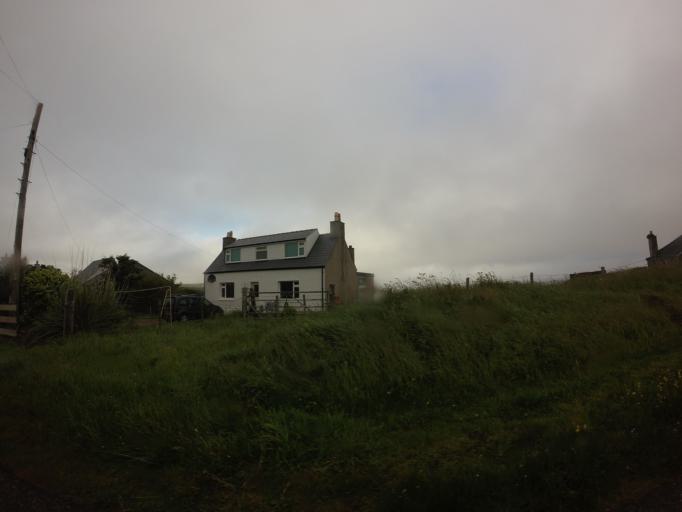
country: GB
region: Scotland
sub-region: Eilean Siar
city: Stornoway
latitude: 58.1971
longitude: -6.2239
